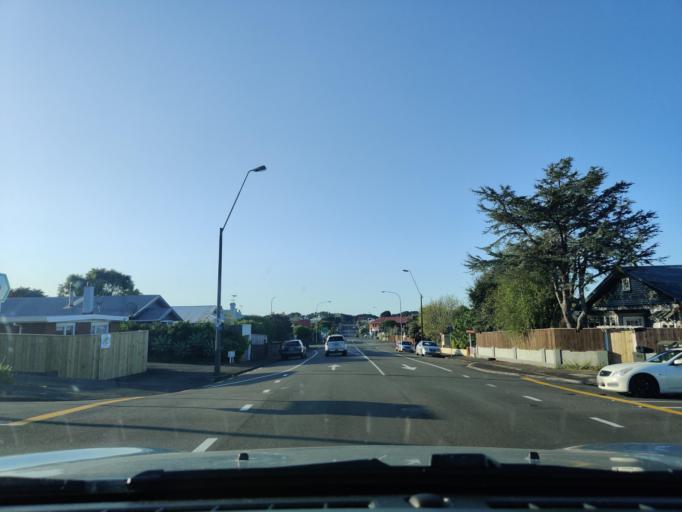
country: NZ
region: Taranaki
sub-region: New Plymouth District
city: New Plymouth
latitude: -39.0629
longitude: 174.0640
